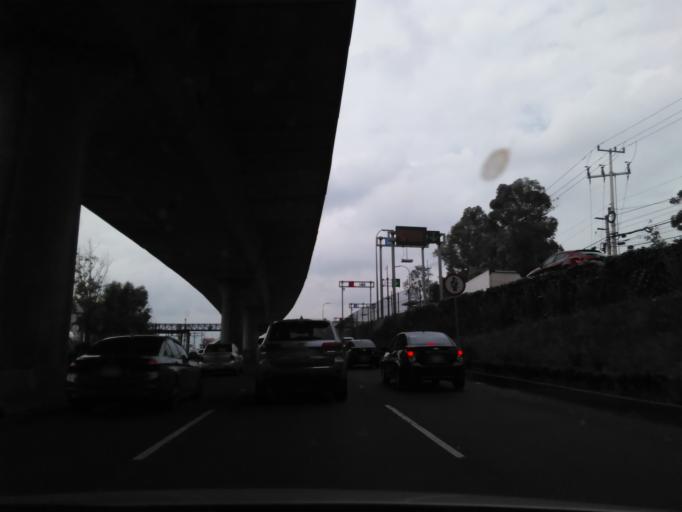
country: MX
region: Mexico City
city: Magdalena Contreras
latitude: 19.3034
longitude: -99.1986
